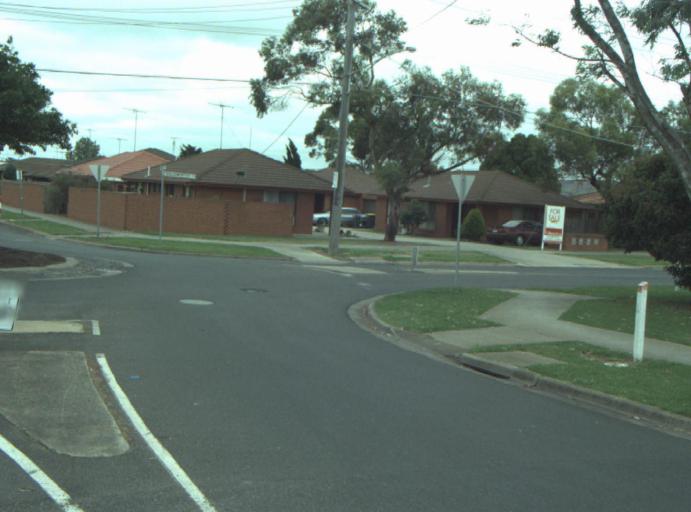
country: AU
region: Victoria
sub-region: Greater Geelong
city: Bell Park
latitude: -38.0769
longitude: 144.3477
